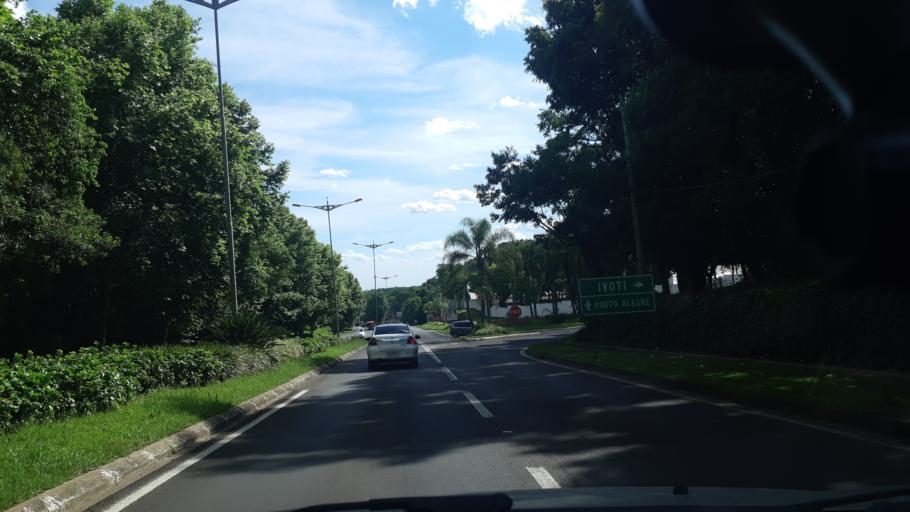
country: BR
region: Rio Grande do Sul
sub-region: Ivoti
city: Ivoti
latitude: -29.6243
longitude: -51.1350
